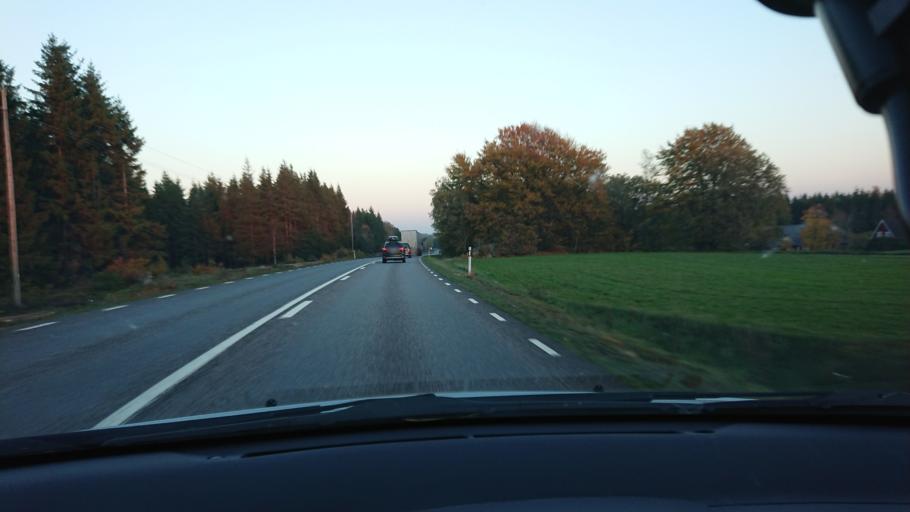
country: SE
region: Halland
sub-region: Laholms Kommun
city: Knared
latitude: 56.7178
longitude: 13.3001
